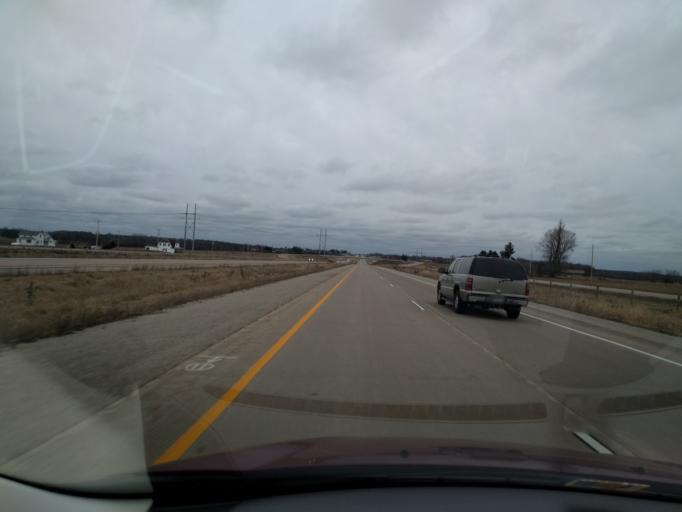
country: US
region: Wisconsin
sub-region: Winnebago County
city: Winneconne
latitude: 44.1751
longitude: -88.6645
